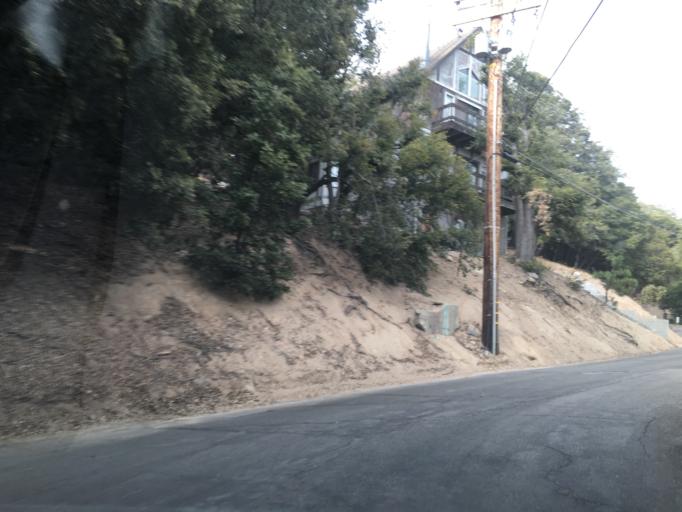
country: US
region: California
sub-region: San Bernardino County
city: Crestline
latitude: 34.2454
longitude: -117.2735
